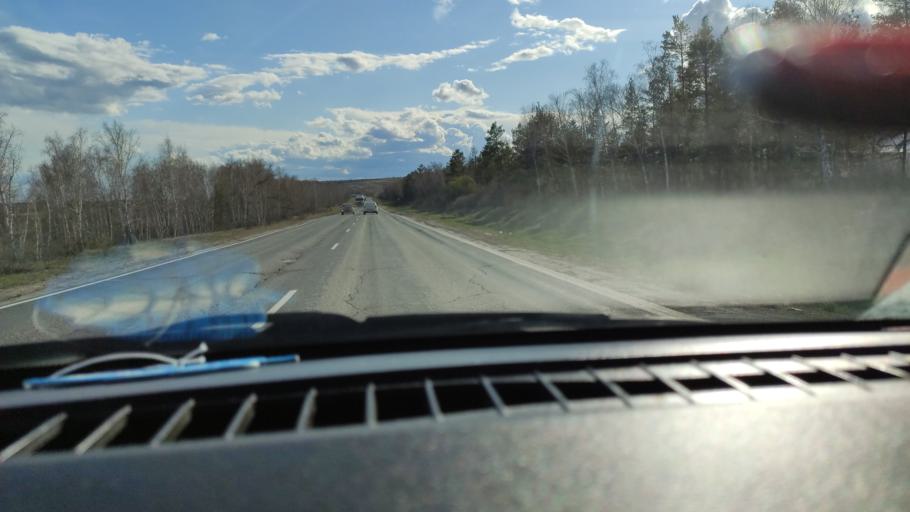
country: RU
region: Saratov
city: Sennoy
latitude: 52.1052
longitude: 46.8206
